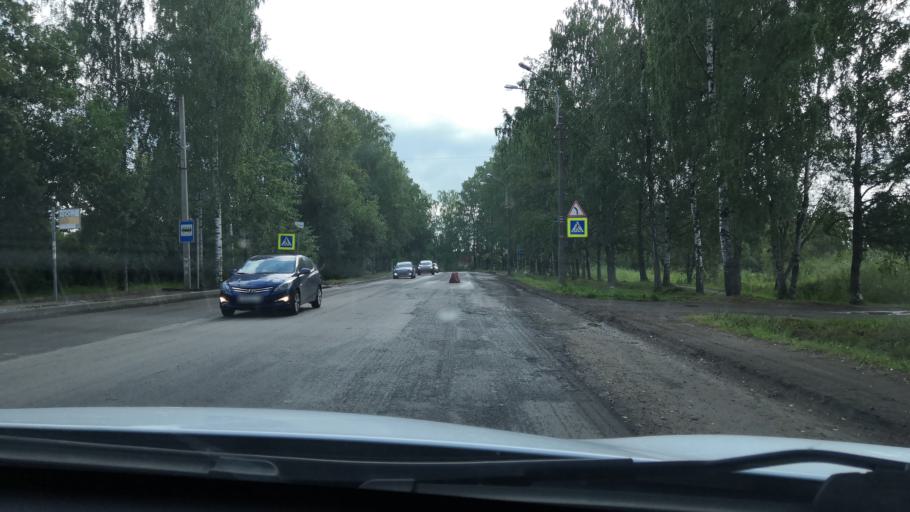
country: RU
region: St.-Petersburg
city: Tyarlevo
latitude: 59.7119
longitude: 30.4515
